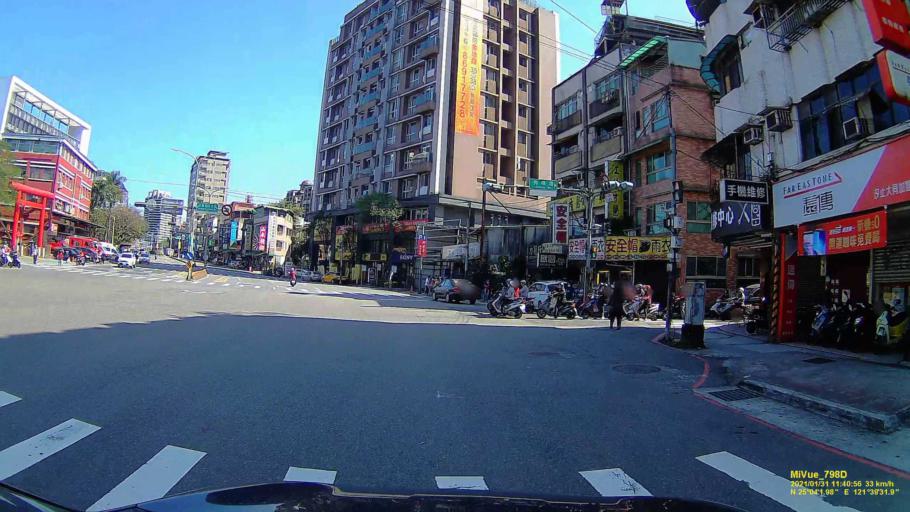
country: TW
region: Taiwan
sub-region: Keelung
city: Keelung
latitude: 25.0672
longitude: 121.6590
